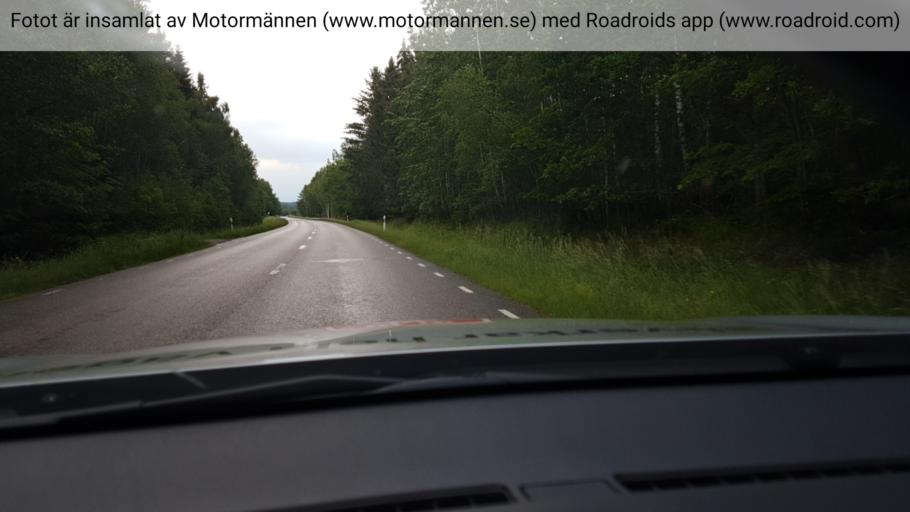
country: SE
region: Vaestra Goetaland
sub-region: Hjo Kommun
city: Hjo
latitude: 58.2011
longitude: 14.2074
